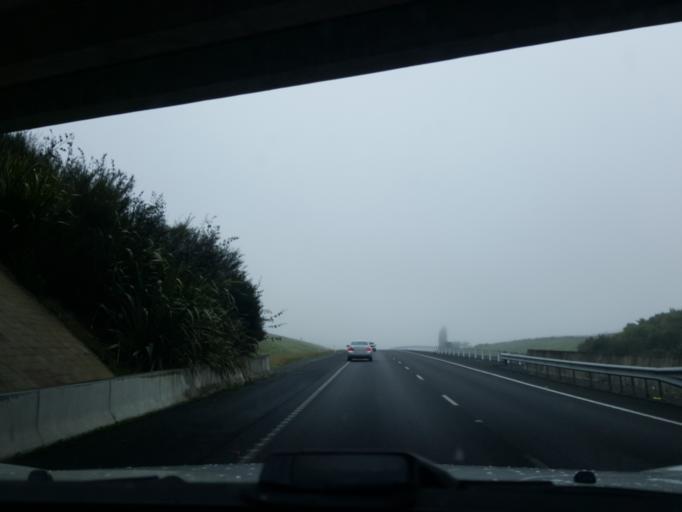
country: NZ
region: Waikato
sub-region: Waikato District
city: Ngaruawahia
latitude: -37.6972
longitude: 175.2117
